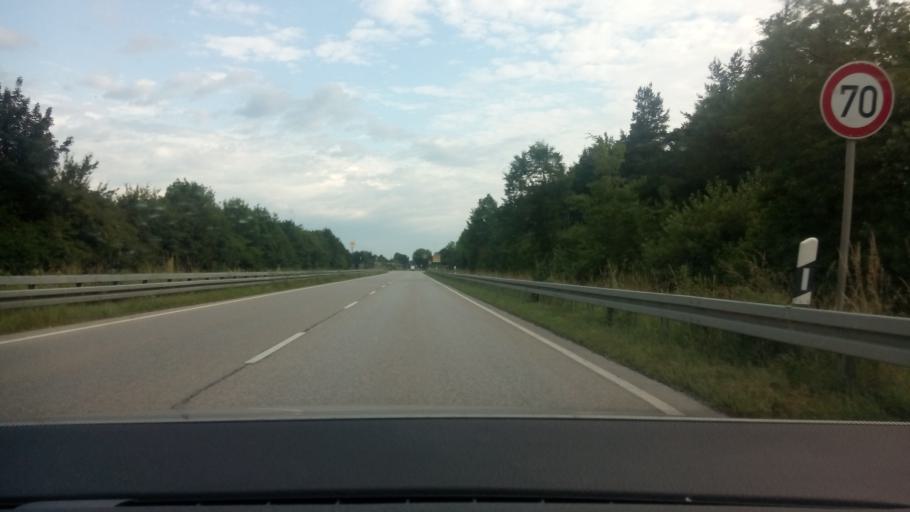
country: DE
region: Bavaria
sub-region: Upper Bavaria
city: Unterschleissheim
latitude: 48.2691
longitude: 11.5931
